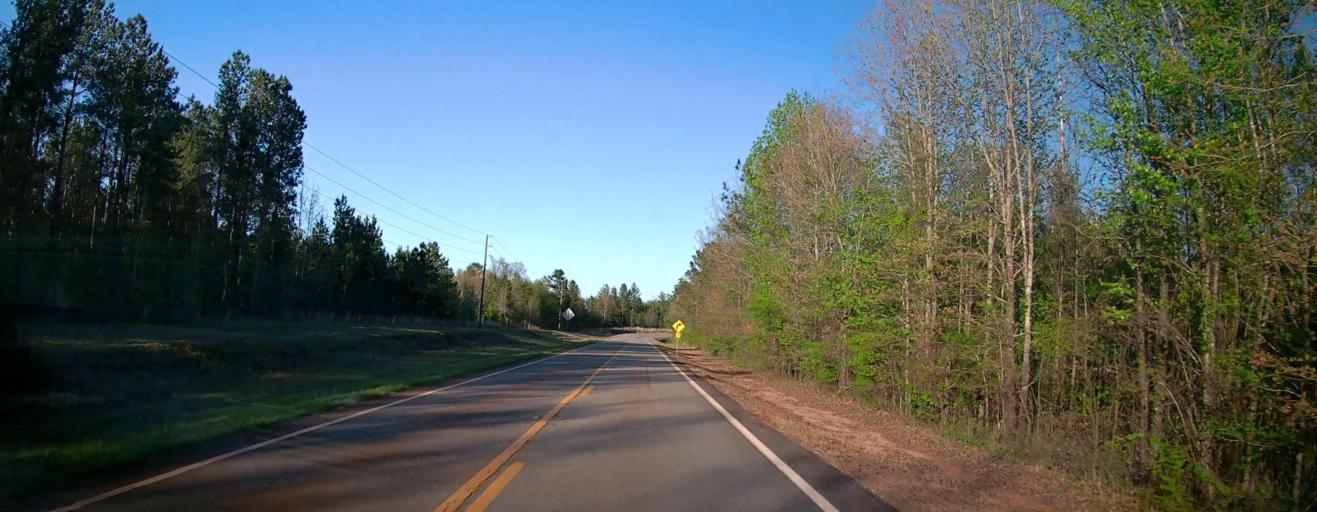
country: US
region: Georgia
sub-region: Wilkinson County
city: Irwinton
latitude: 32.8735
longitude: -83.1019
